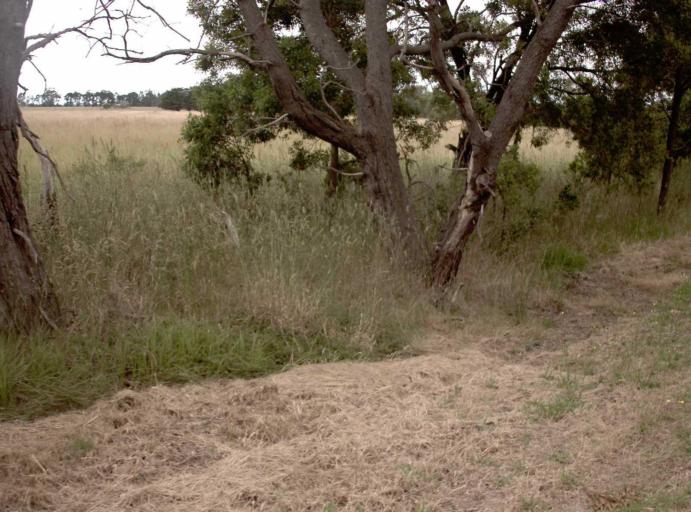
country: AU
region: Victoria
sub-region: Latrobe
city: Traralgon
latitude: -38.4939
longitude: 146.8194
